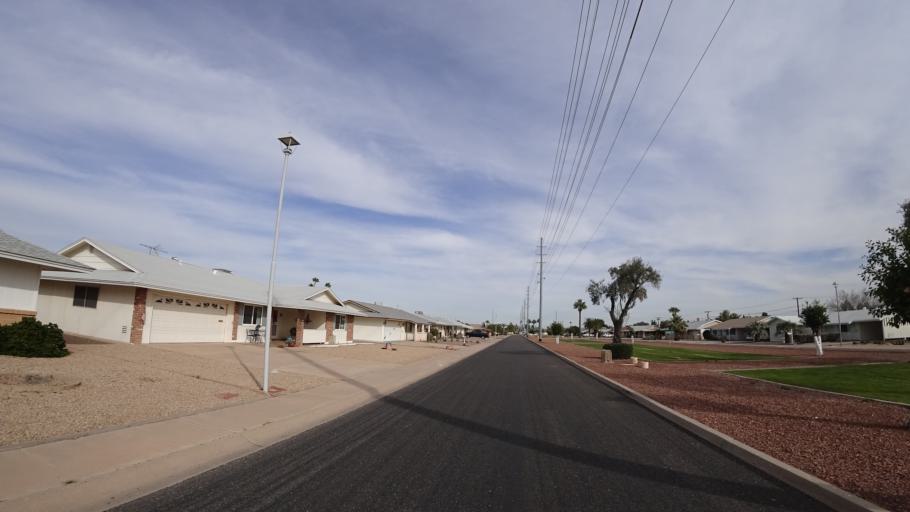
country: US
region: Arizona
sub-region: Maricopa County
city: Sun City
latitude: 33.5949
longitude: -112.2761
